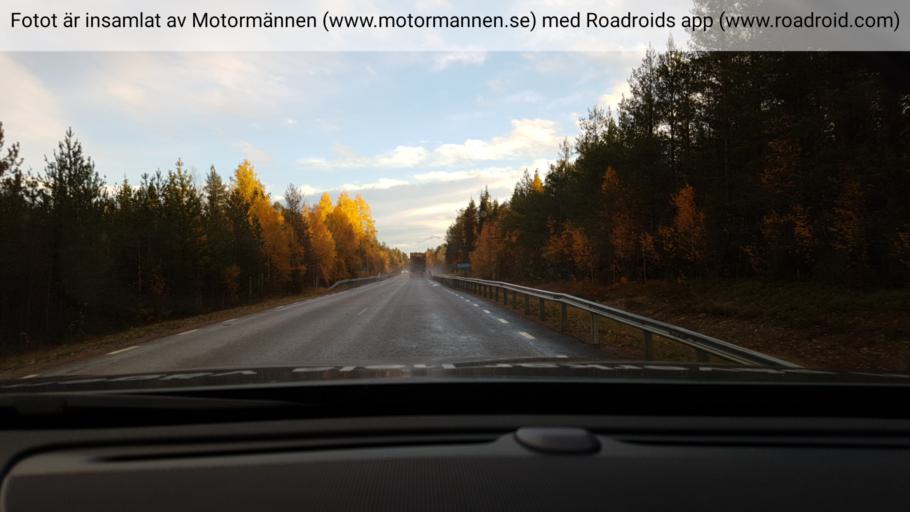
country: SE
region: Norrbotten
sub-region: Overkalix Kommun
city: OEverkalix
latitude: 66.6949
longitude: 22.6699
